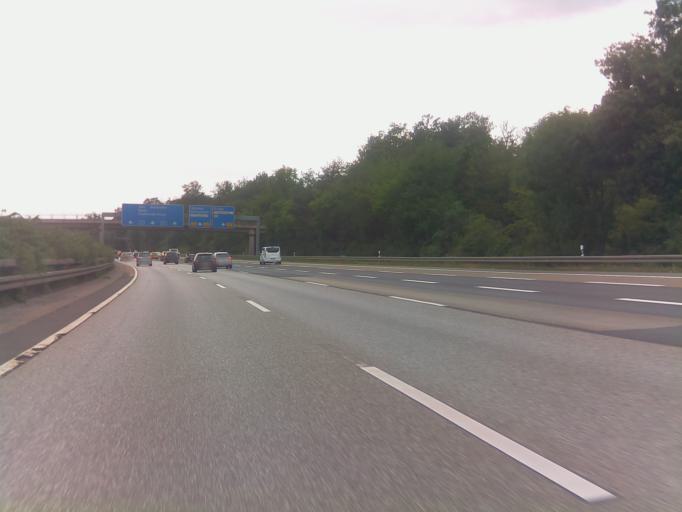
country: DE
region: Hesse
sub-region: Regierungsbezirk Darmstadt
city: Neu Isenburg
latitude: 50.0604
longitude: 8.6590
